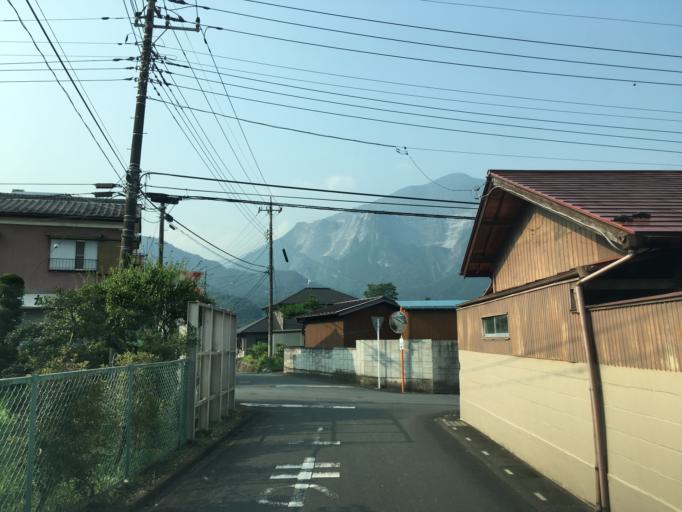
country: JP
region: Saitama
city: Chichibu
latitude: 35.9836
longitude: 139.1115
